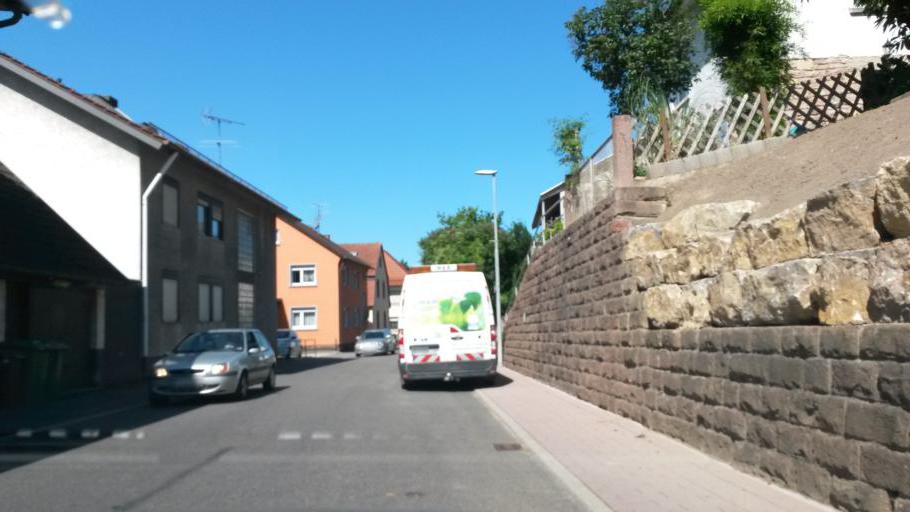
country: DE
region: Baden-Wuerttemberg
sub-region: Karlsruhe Region
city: Ispringen
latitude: 48.9304
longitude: 8.6428
